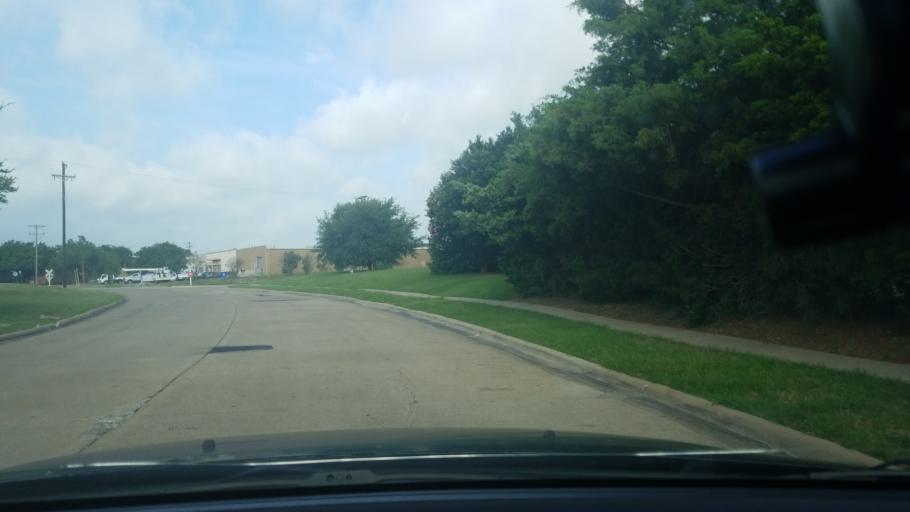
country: US
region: Texas
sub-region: Dallas County
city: Mesquite
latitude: 32.7748
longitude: -96.6510
